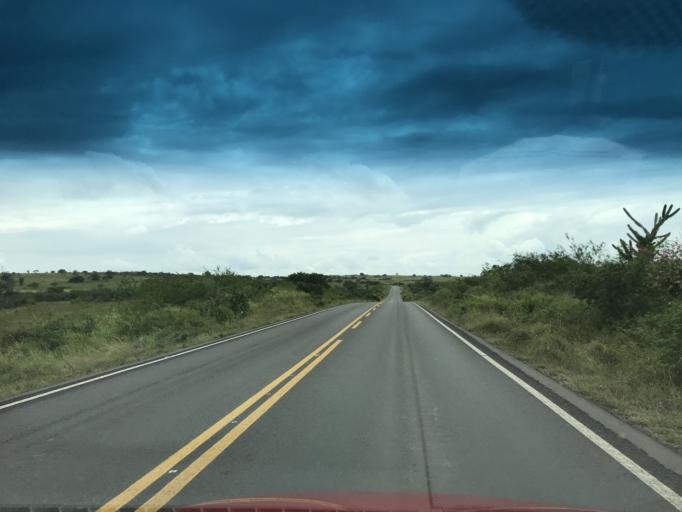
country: BR
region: Bahia
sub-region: Castro Alves
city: Castro Alves
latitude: -12.7561
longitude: -39.4132
